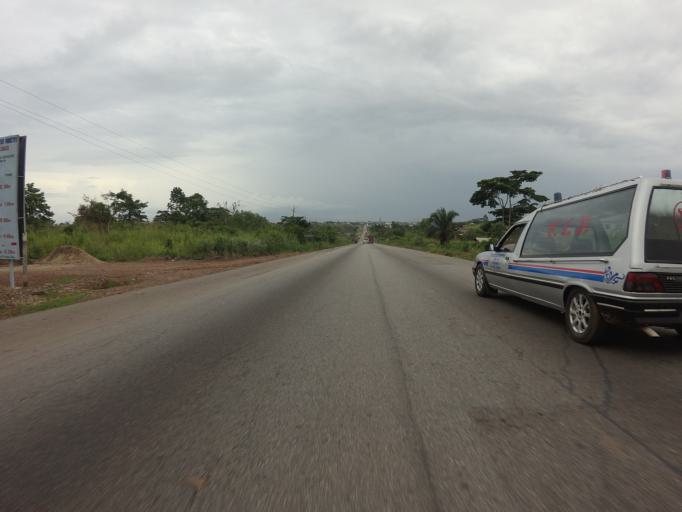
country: GH
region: Ashanti
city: Konongo
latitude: 6.6162
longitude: -1.1648
